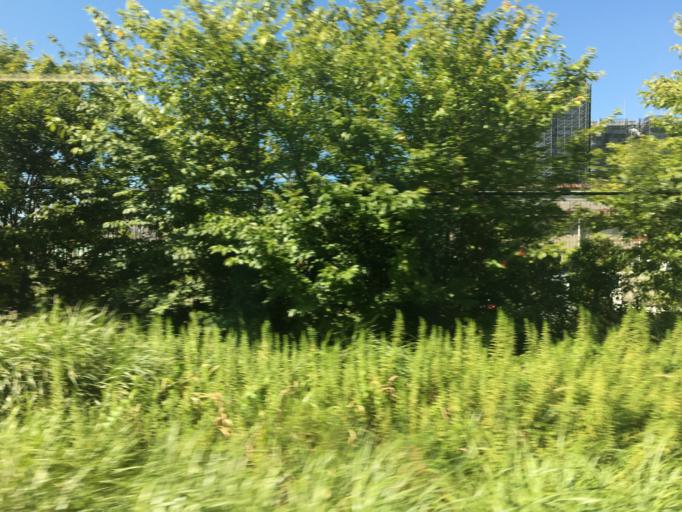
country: JP
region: Kanagawa
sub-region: Kawasaki-shi
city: Kawasaki
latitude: 35.5482
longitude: 139.6730
